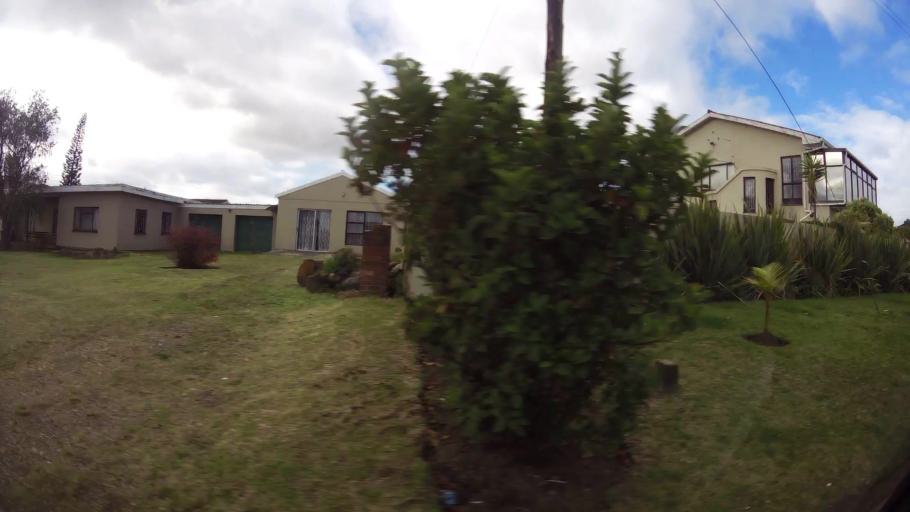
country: ZA
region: Western Cape
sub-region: Eden District Municipality
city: George
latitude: -34.0085
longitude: 22.4395
